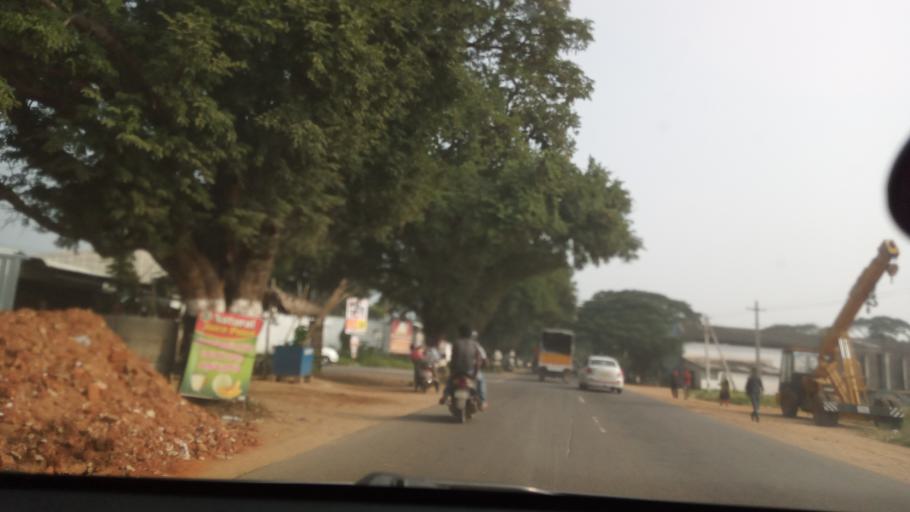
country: IN
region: Tamil Nadu
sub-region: Coimbatore
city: Annur
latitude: 11.1798
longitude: 77.0601
